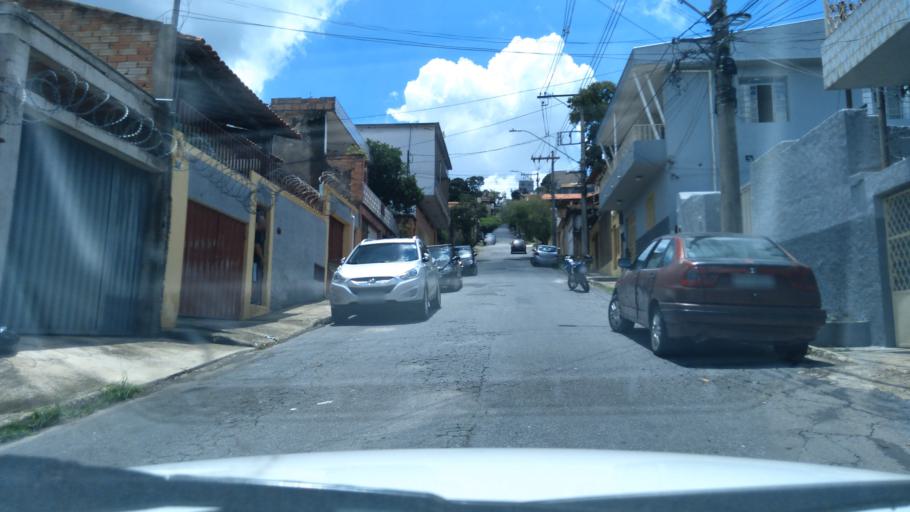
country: BR
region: Minas Gerais
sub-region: Belo Horizonte
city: Belo Horizonte
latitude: -19.9218
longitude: -43.9018
